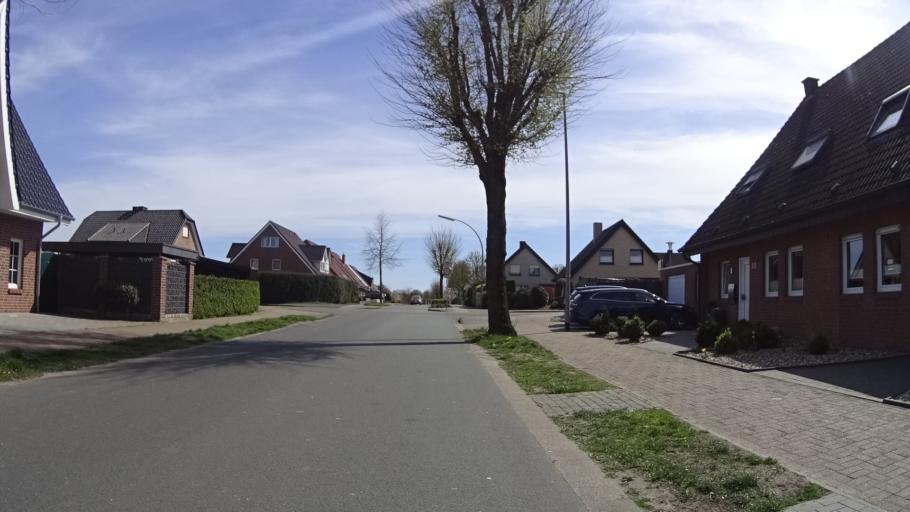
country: DE
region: North Rhine-Westphalia
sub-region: Regierungsbezirk Munster
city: Dreierwalde
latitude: 52.2925
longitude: 7.4711
